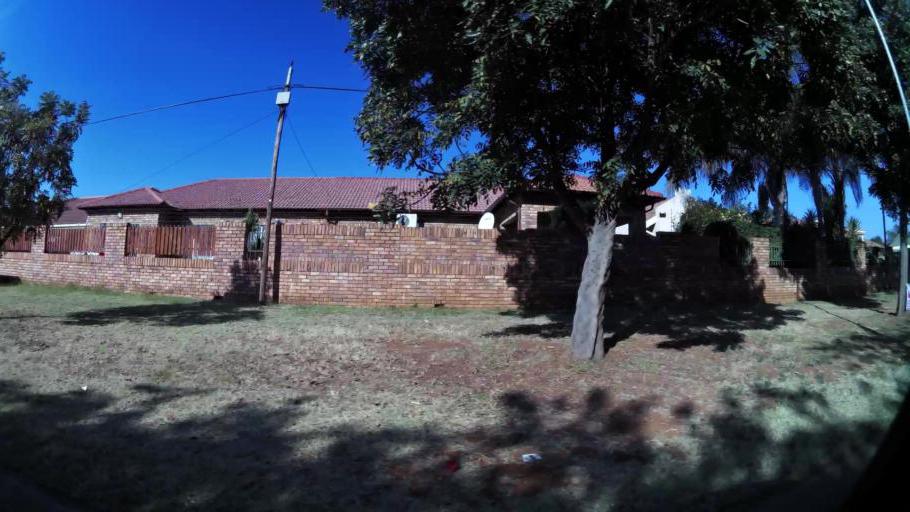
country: ZA
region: Gauteng
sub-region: City of Tshwane Metropolitan Municipality
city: Pretoria
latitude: -25.6697
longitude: 28.1498
